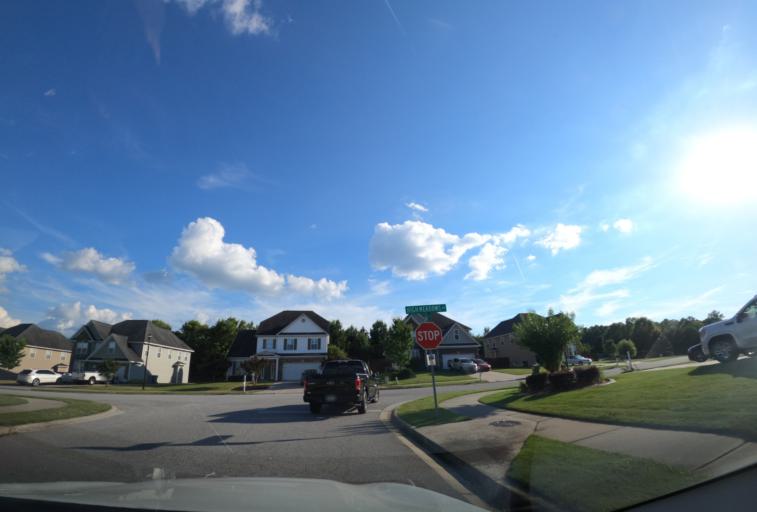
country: US
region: Georgia
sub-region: Columbia County
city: Grovetown
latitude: 33.5082
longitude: -82.2364
